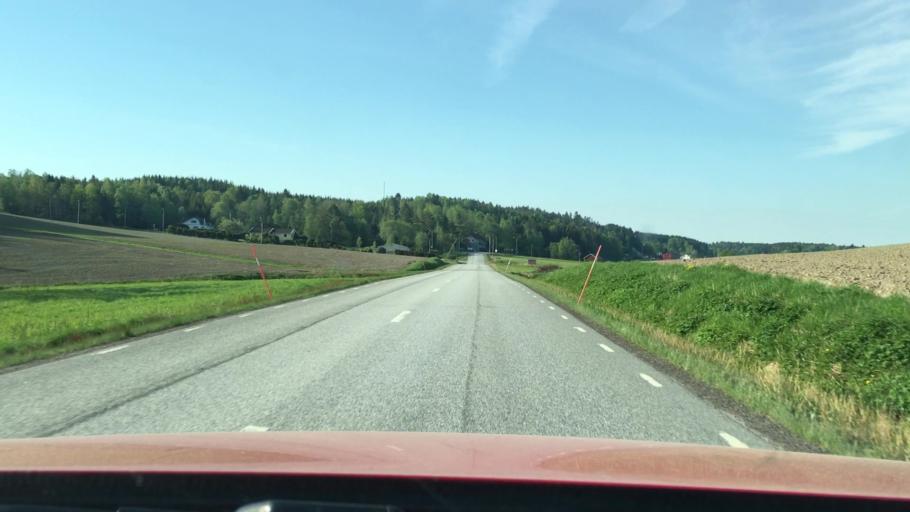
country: SE
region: Vaestra Goetaland
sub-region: Munkedals Kommun
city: Munkedal
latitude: 58.6090
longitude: 11.5589
